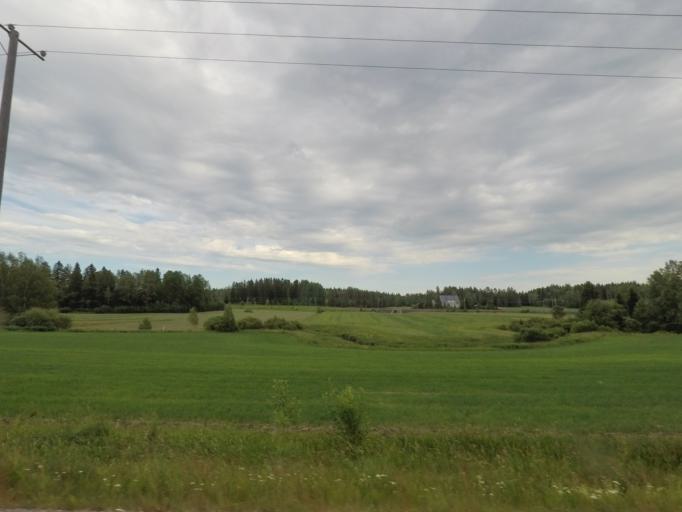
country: FI
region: Uusimaa
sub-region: Helsinki
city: Maentsaelae
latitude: 60.6870
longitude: 25.3710
